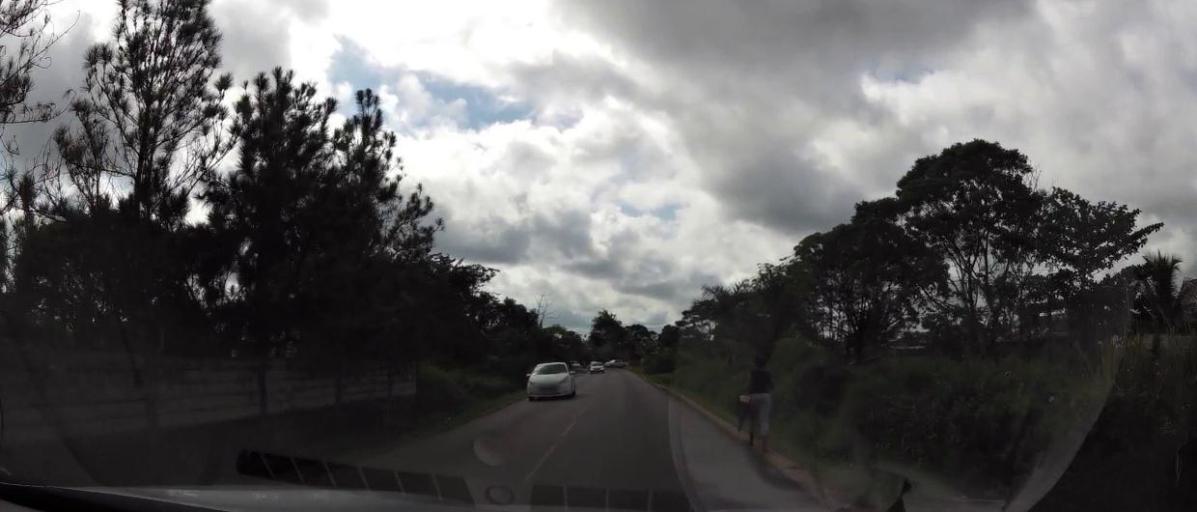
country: GF
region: Guyane
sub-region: Guyane
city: Matoury
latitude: 4.8738
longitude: -52.3279
